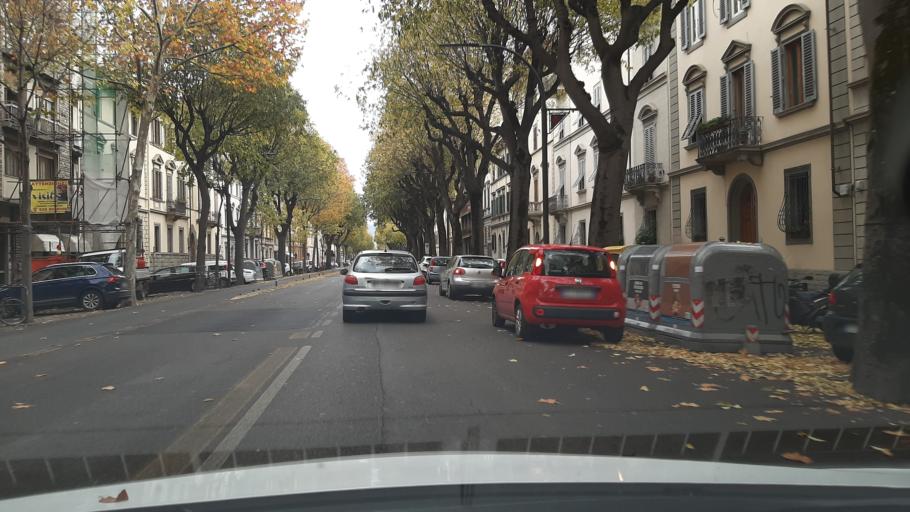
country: IT
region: Tuscany
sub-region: Province of Florence
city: Fiesole
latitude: 43.7828
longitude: 11.2754
